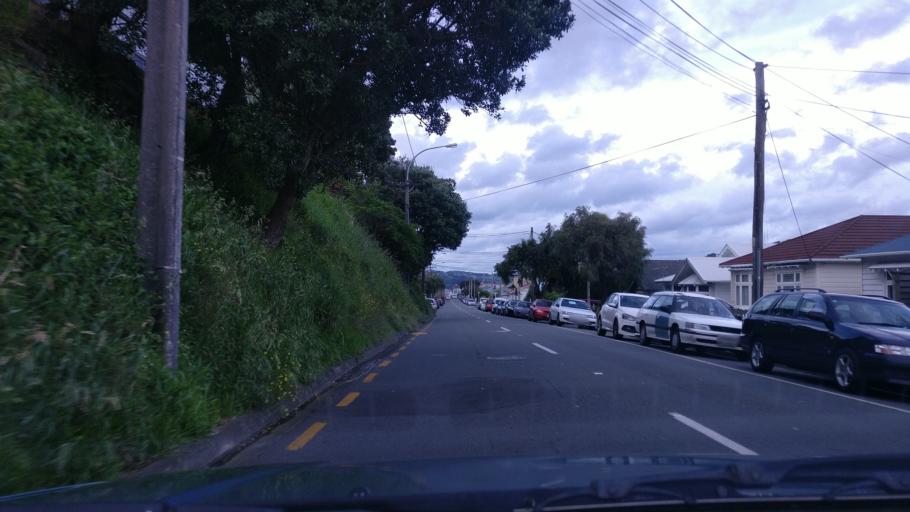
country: NZ
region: Wellington
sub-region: Wellington City
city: Brooklyn
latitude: -41.3133
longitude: 174.7759
